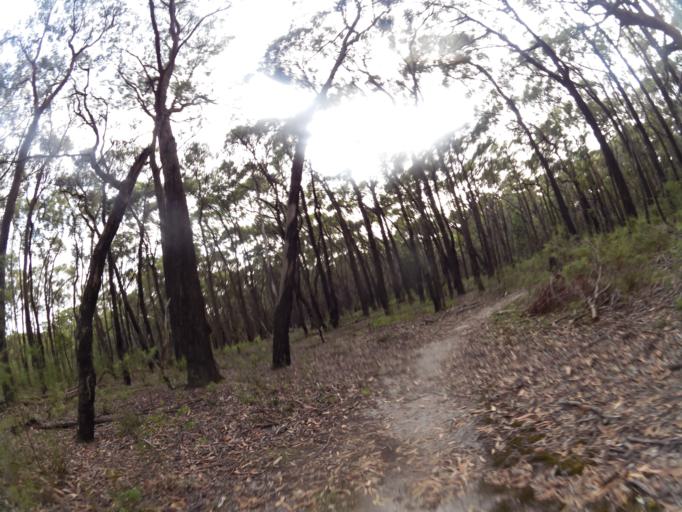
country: AU
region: Victoria
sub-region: Colac-Otway
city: Colac
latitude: -38.4924
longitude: 143.6970
